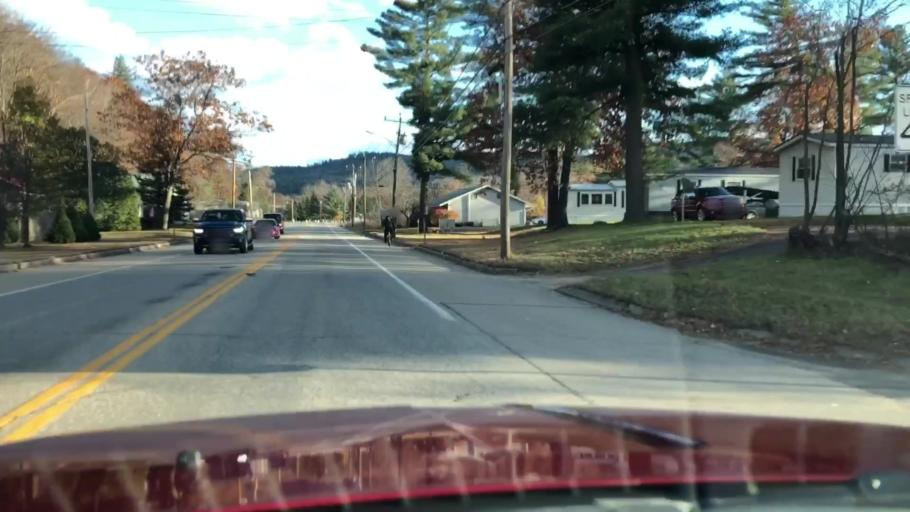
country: US
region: Maine
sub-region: Oxford County
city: Mexico
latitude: 44.5387
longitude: -70.5151
